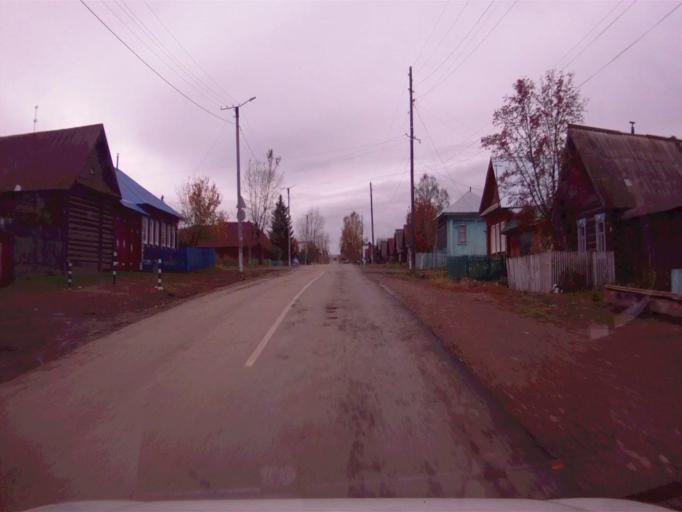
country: RU
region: Chelyabinsk
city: Nyazepetrovsk
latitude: 56.0601
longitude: 59.5804
